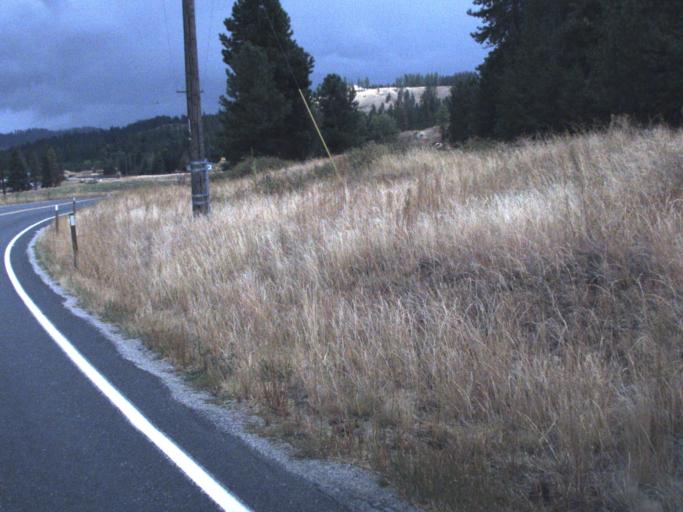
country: US
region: Washington
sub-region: Stevens County
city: Chewelah
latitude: 48.1432
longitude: -117.7307
